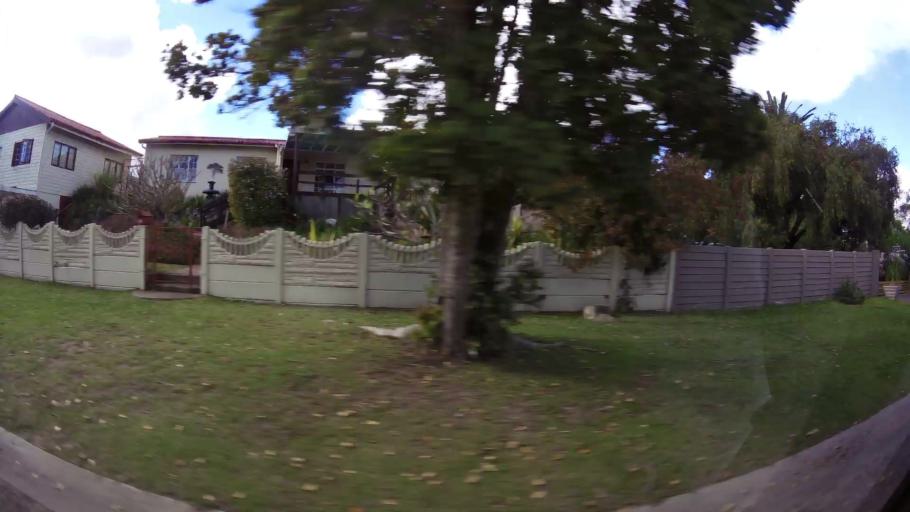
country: ZA
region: Western Cape
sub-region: Eden District Municipality
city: Knysna
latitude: -34.0441
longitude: 23.0730
